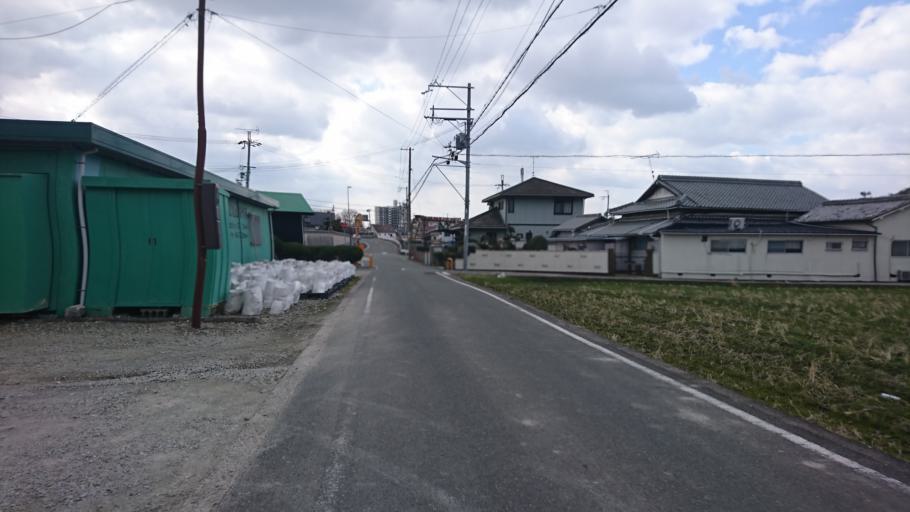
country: JP
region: Hyogo
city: Kakogawacho-honmachi
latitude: 34.7966
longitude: 134.8077
